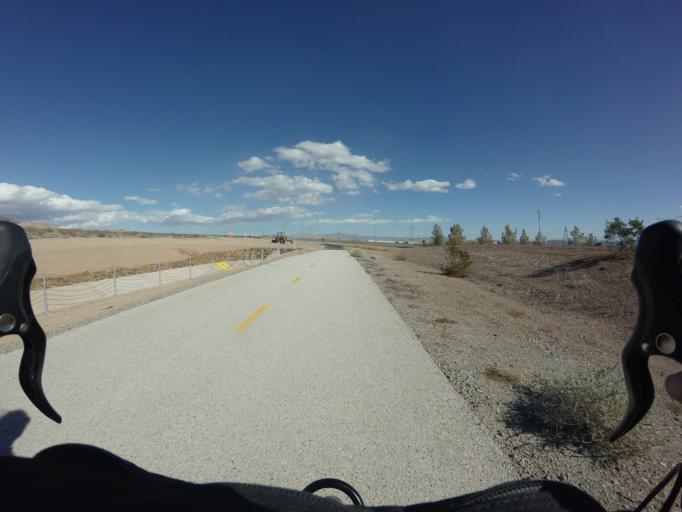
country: US
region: Nevada
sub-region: Clark County
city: Boulder City
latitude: 35.9722
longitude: -114.8691
